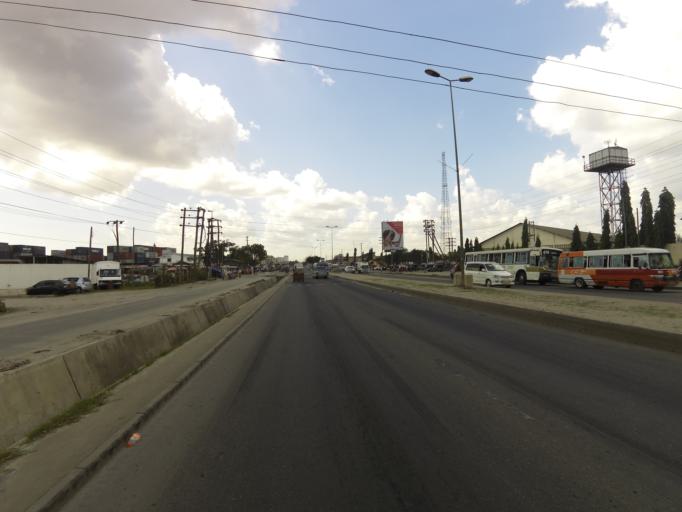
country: TZ
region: Dar es Salaam
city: Magomeni
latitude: -6.8157
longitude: 39.2210
